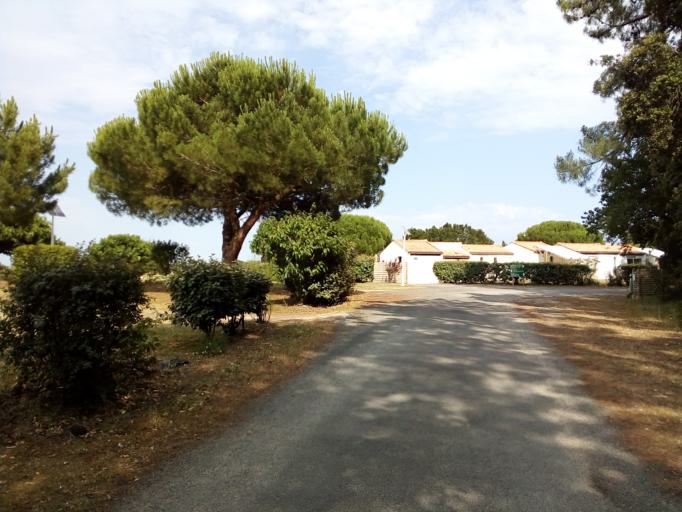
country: FR
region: Poitou-Charentes
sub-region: Departement de la Charente-Maritime
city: Boyard-Ville
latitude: 45.9513
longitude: -1.2450
